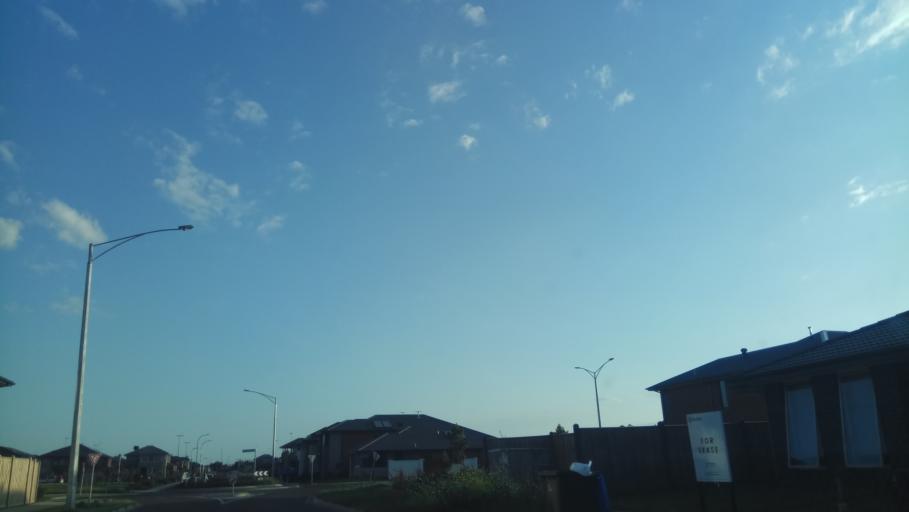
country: AU
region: Victoria
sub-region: Wyndham
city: Point Cook
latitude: -37.9015
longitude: 144.7569
